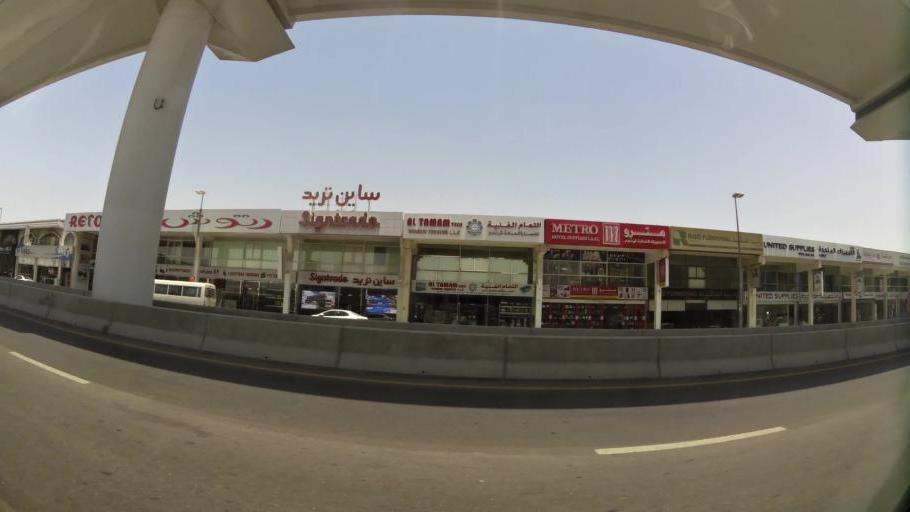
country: AE
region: Ash Shariqah
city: Sharjah
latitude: 25.2710
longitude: 55.3346
